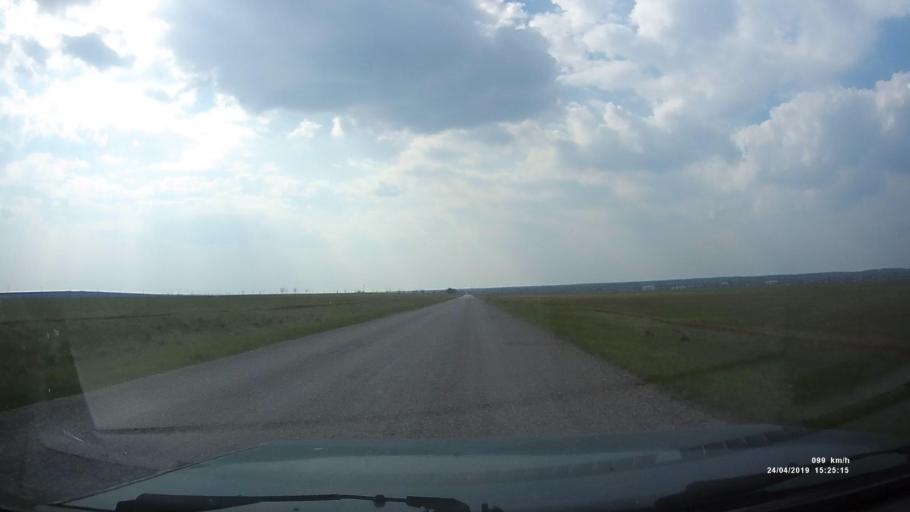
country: RU
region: Rostov
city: Remontnoye
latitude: 46.5514
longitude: 43.0526
